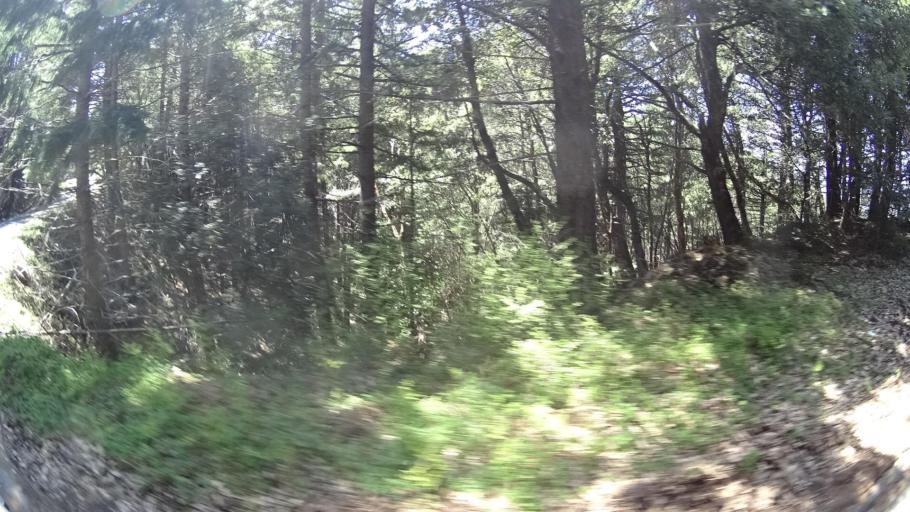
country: US
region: California
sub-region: Humboldt County
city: Rio Dell
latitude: 40.2831
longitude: -124.0647
